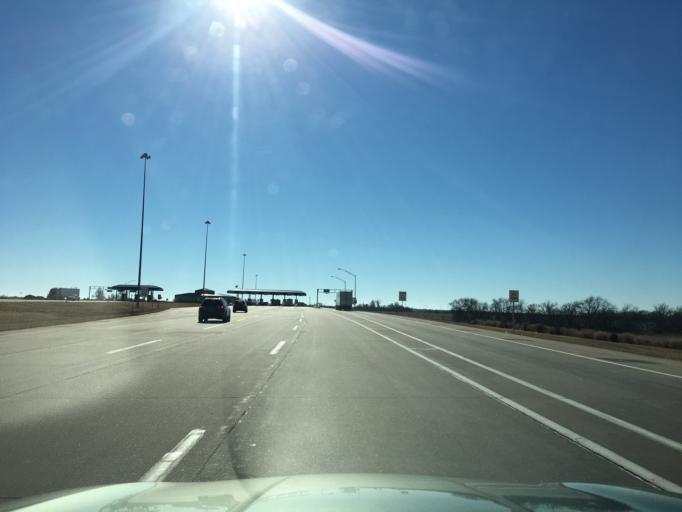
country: US
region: Kansas
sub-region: Sumner County
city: Wellington
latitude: 37.2418
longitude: -97.3392
